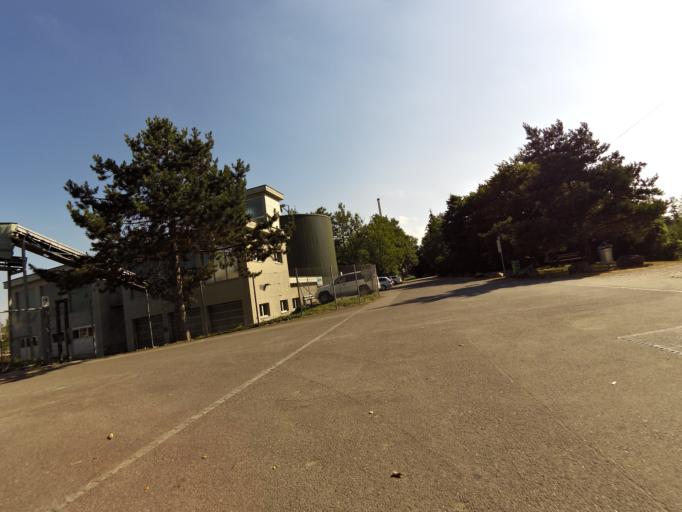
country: CH
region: Aargau
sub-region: Bezirk Lenzburg
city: Niederlenz
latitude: 47.4181
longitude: 8.1629
